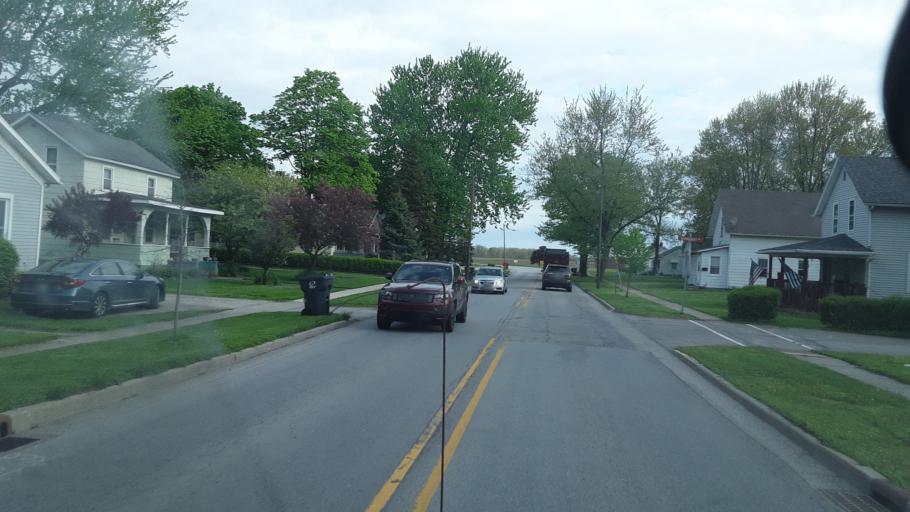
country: US
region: Indiana
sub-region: Whitley County
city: Churubusco
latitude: 41.2356
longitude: -85.3226
